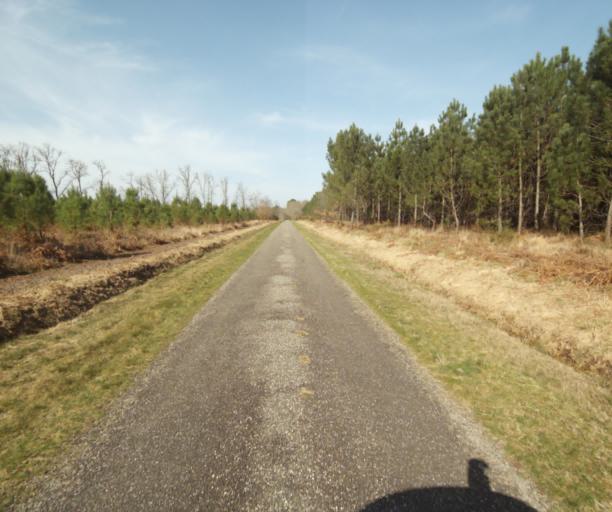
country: FR
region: Aquitaine
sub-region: Departement des Landes
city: Roquefort
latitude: 44.1447
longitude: -0.2048
